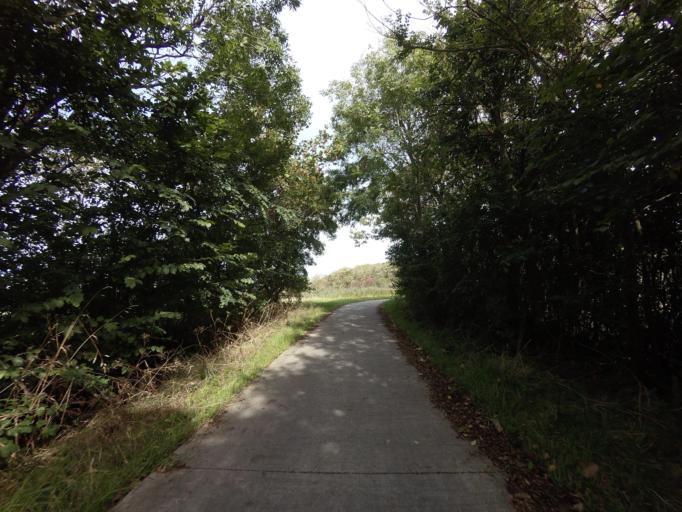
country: NL
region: North Holland
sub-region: Gemeente Texel
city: Den Burg
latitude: 53.0812
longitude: 4.7847
